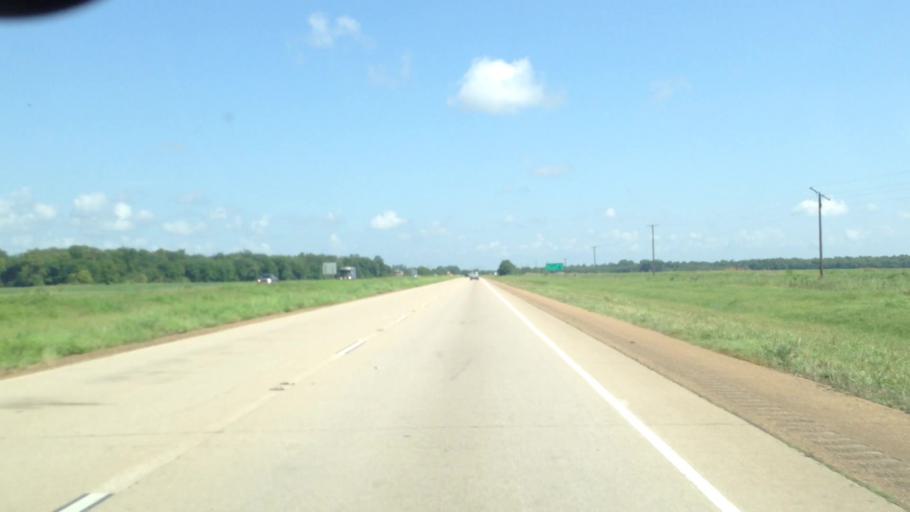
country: US
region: Louisiana
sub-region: Rapides Parish
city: Woodworth
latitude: 31.1764
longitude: -92.4663
